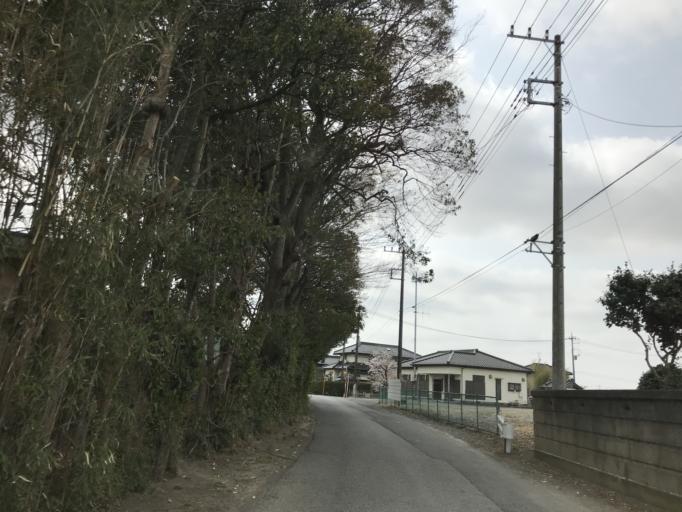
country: JP
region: Ibaraki
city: Mitsukaido
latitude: 36.0260
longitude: 140.0071
